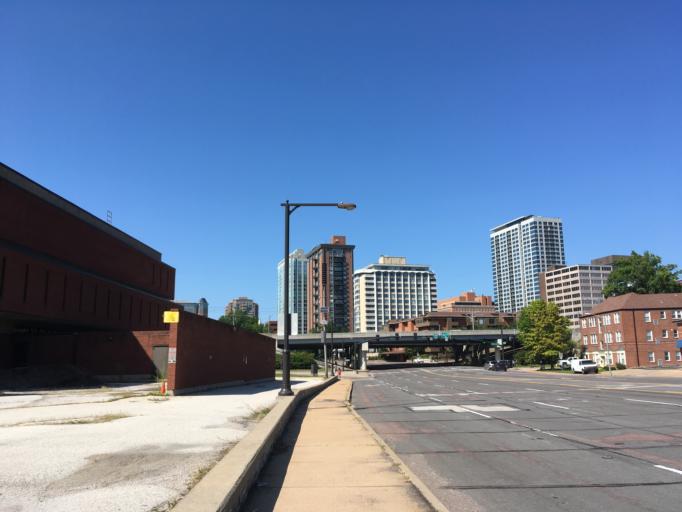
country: US
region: Missouri
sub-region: Saint Louis County
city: Clayton
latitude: 38.6444
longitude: -90.3431
